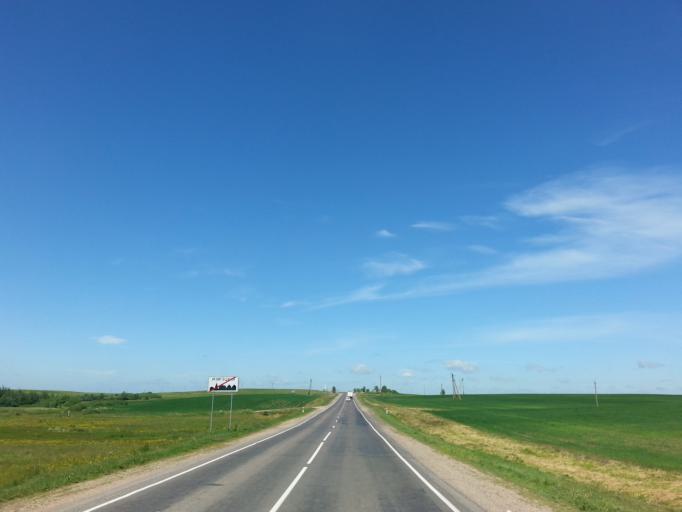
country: BY
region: Vitebsk
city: Hlybokaye
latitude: 55.2063
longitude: 27.6208
